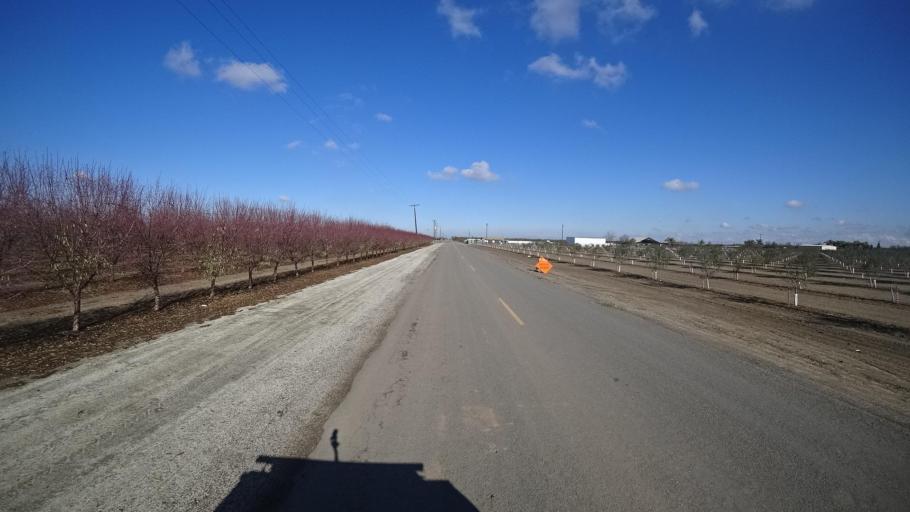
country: US
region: California
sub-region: Kern County
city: McFarland
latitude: 35.6656
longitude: -119.2588
